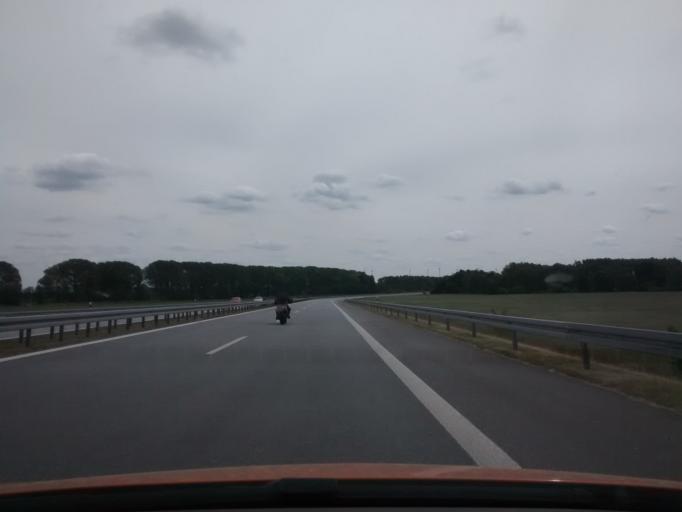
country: DE
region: Brandenburg
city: Trebbin
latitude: 52.2263
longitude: 13.2455
